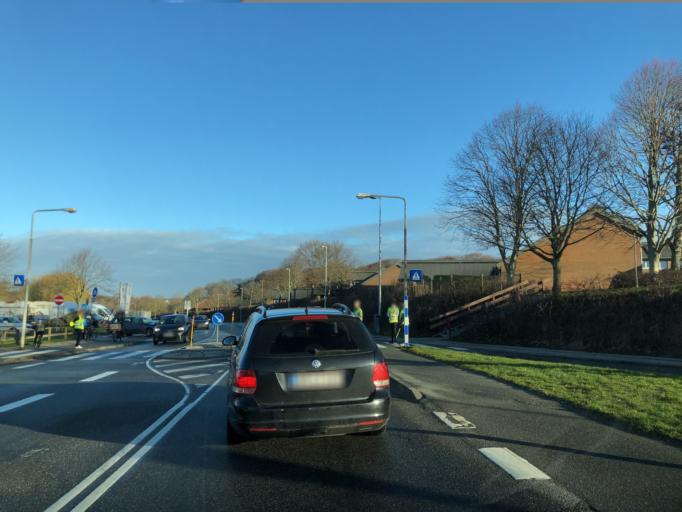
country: DK
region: Central Jutland
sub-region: Favrskov Kommune
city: Hinnerup
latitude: 56.2598
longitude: 10.0701
